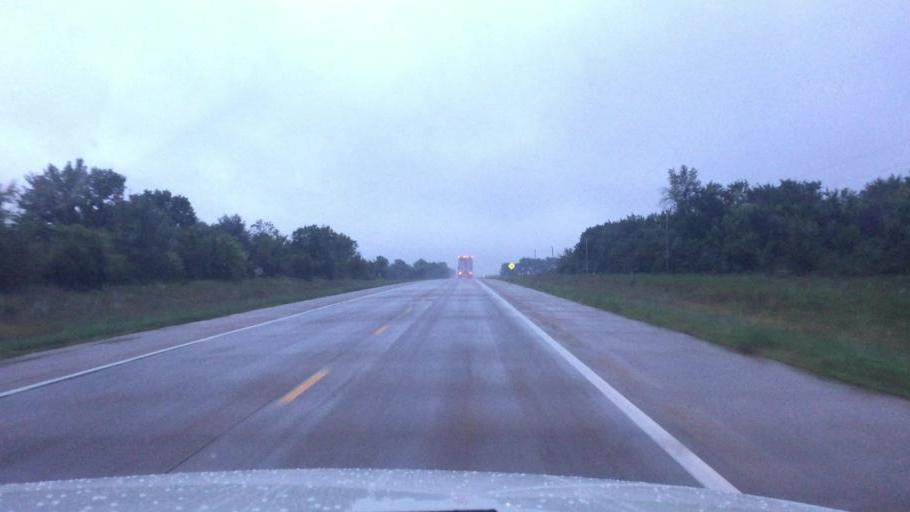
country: US
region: Kansas
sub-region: Neosho County
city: Chanute
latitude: 37.5467
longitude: -95.4708
